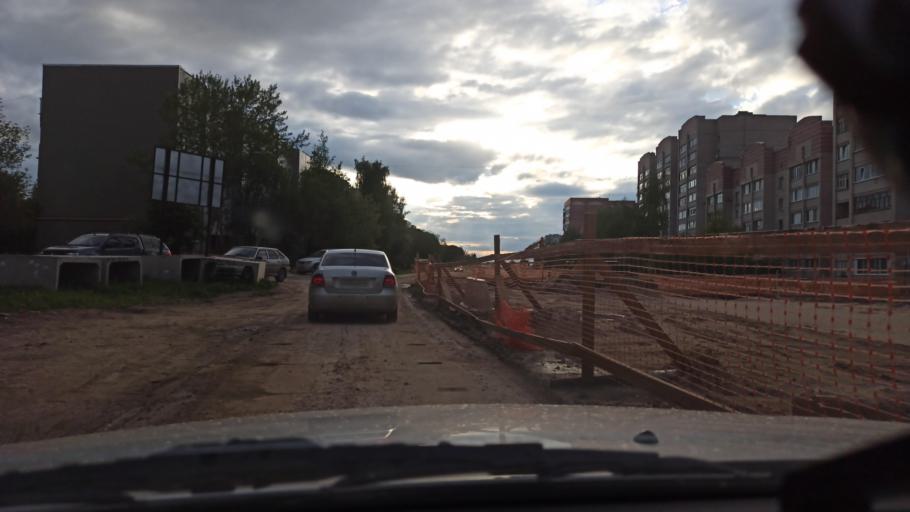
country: RU
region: Vologda
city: Vologda
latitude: 59.1952
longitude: 39.8768
